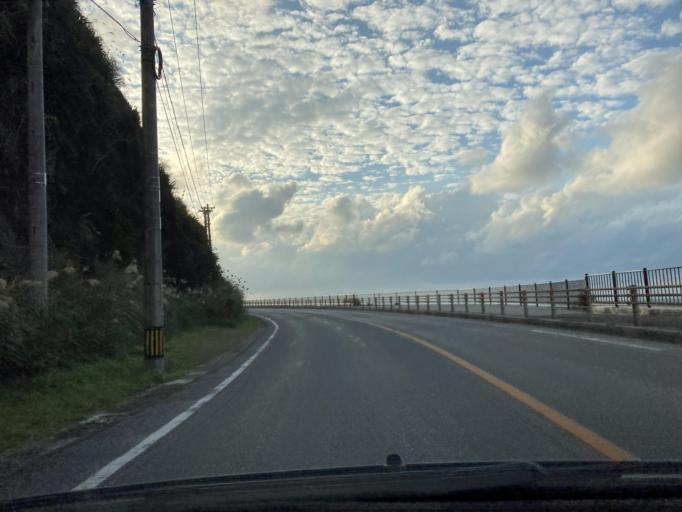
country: JP
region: Okinawa
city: Nago
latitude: 26.7974
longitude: 128.2283
